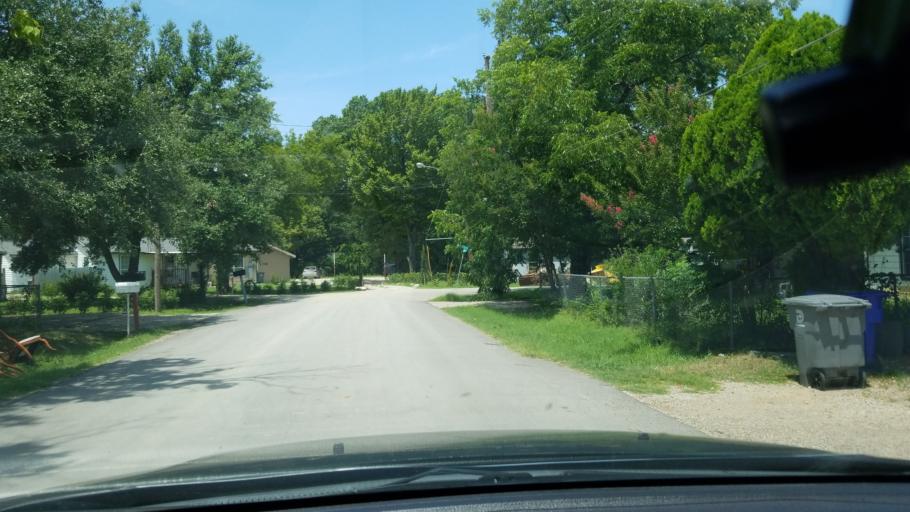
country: US
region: Texas
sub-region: Dallas County
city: Balch Springs
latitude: 32.7453
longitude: -96.6419
